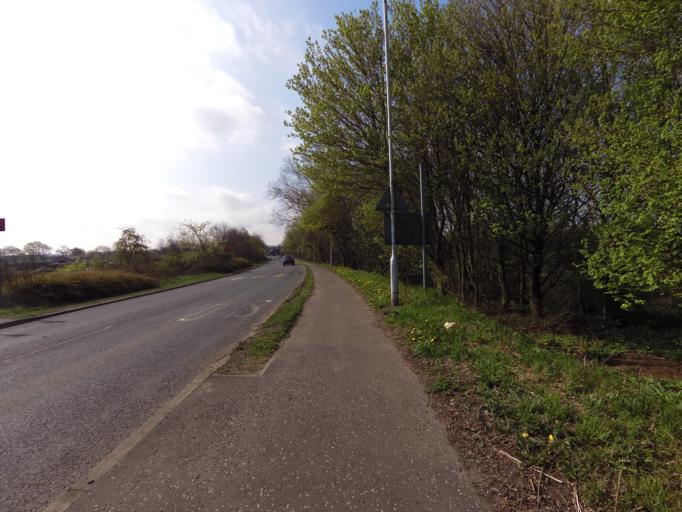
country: GB
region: Scotland
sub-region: Fife
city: Thornton
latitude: 56.1732
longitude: -3.1455
